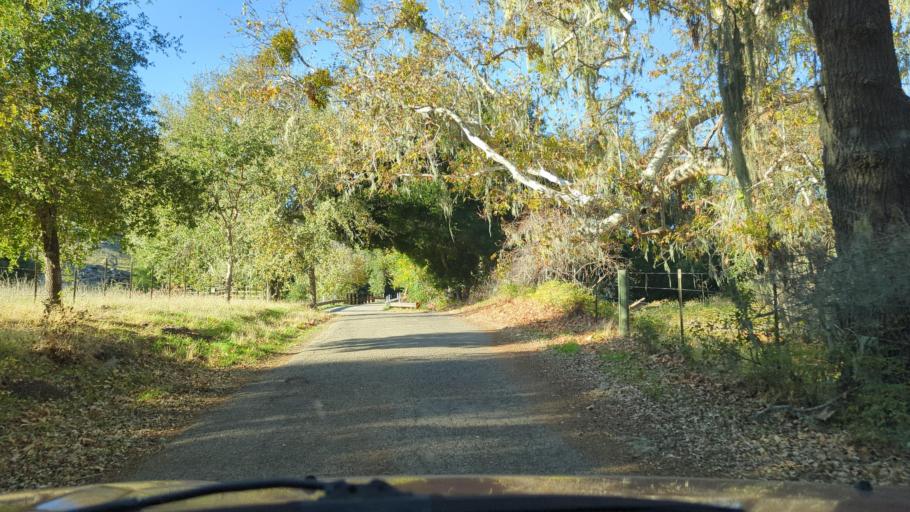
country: US
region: California
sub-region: Santa Barbara County
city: Santa Ynez
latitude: 34.5664
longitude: -120.0947
